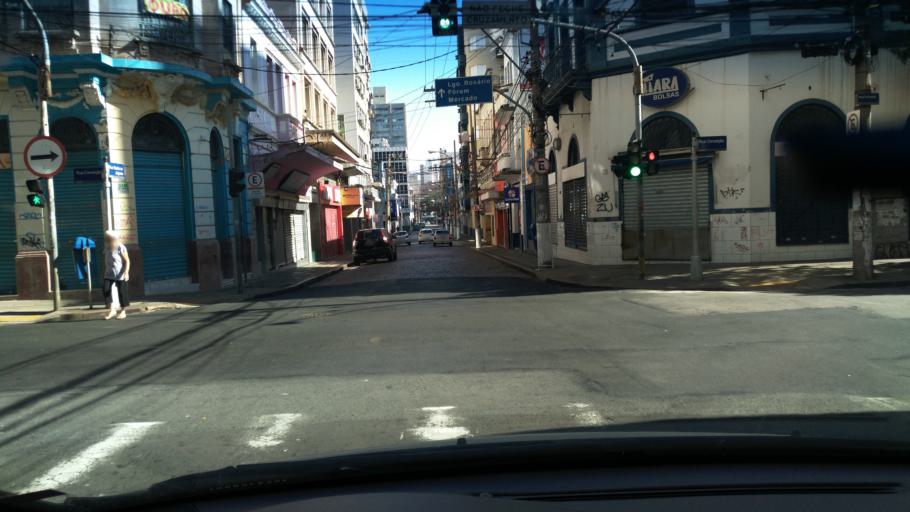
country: BR
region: Sao Paulo
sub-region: Campinas
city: Campinas
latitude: -22.9053
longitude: -47.0586
